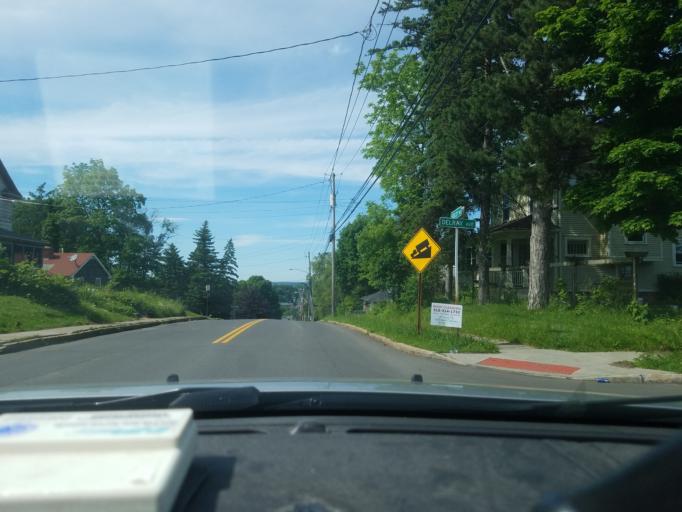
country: US
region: New York
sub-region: Onondaga County
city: East Syracuse
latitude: 43.0497
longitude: -76.1037
